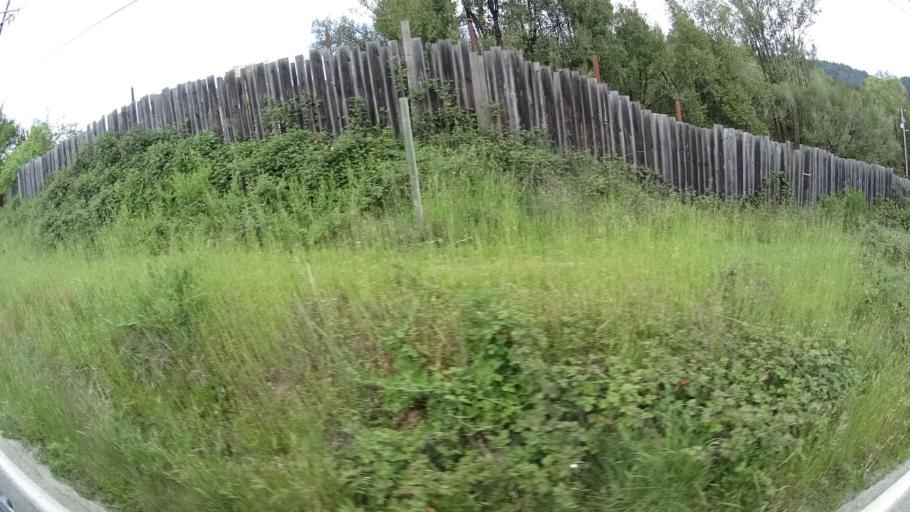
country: US
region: California
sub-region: Humboldt County
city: Redway
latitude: 40.1085
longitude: -123.8993
